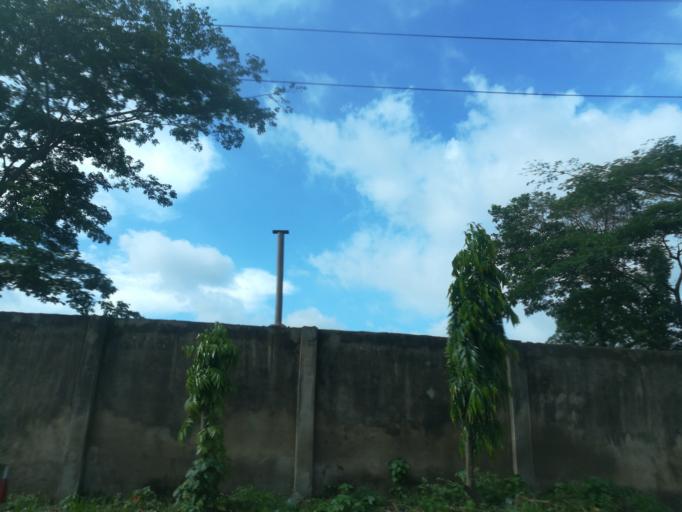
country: NG
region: Lagos
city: Ikeja
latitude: 6.6204
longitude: 3.3570
